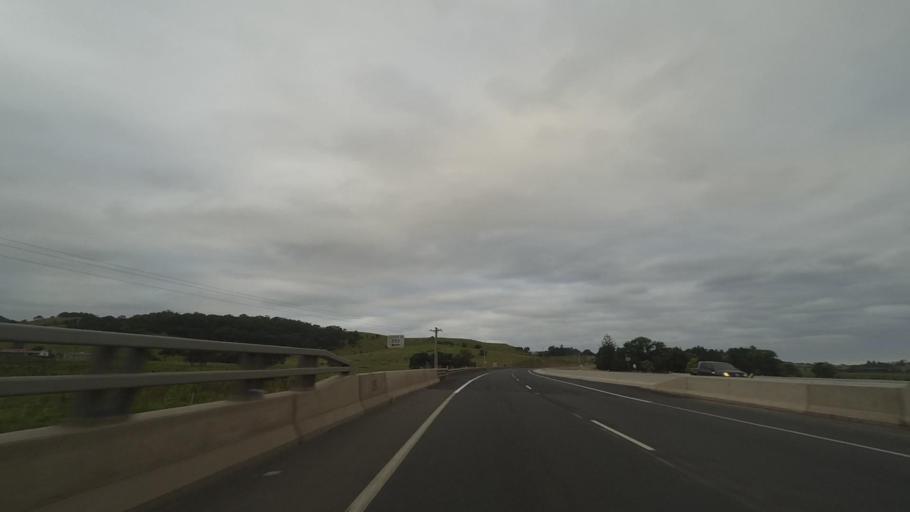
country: AU
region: New South Wales
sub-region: Kiama
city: Gerringong
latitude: -34.7499
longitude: 150.7887
